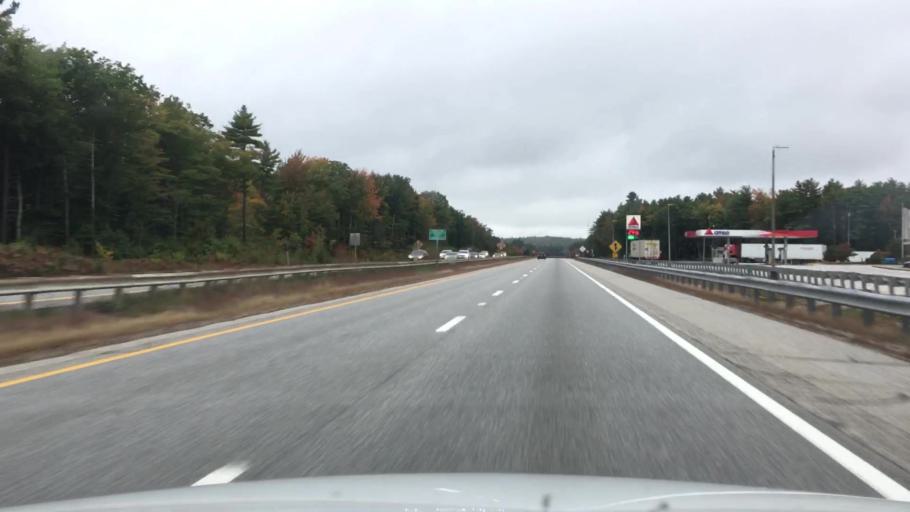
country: US
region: Maine
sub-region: Cumberland County
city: Cumberland Center
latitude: 43.8233
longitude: -70.3205
